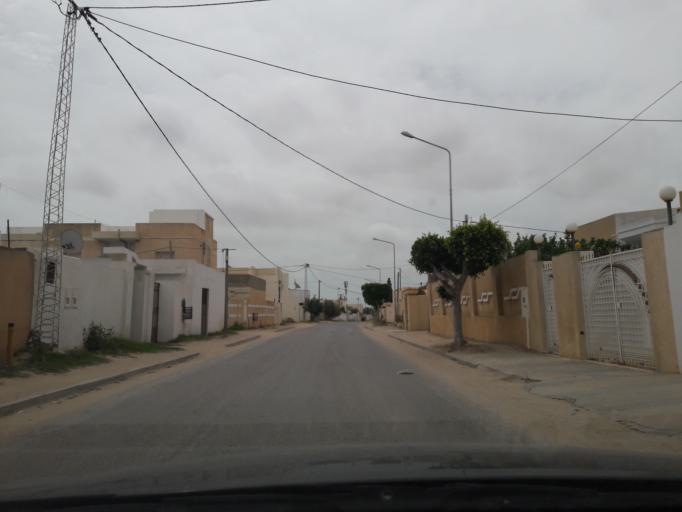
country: TN
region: Safaqis
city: Al Qarmadah
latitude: 34.7964
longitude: 10.7525
